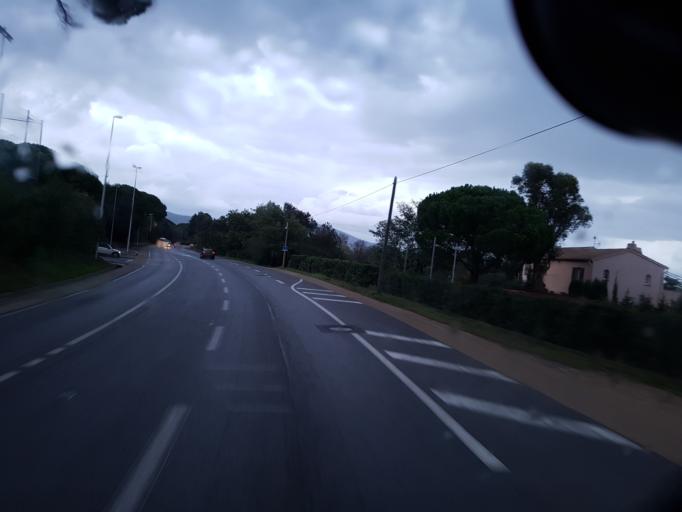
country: FR
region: Provence-Alpes-Cote d'Azur
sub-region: Departement du Var
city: Gassin
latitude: 43.2535
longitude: 6.5745
